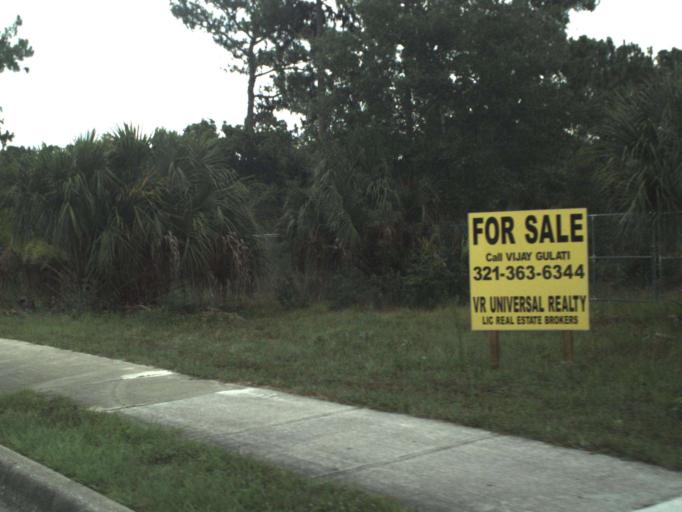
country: US
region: Florida
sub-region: Seminole County
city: Winter Springs
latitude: 28.6988
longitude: -81.3035
